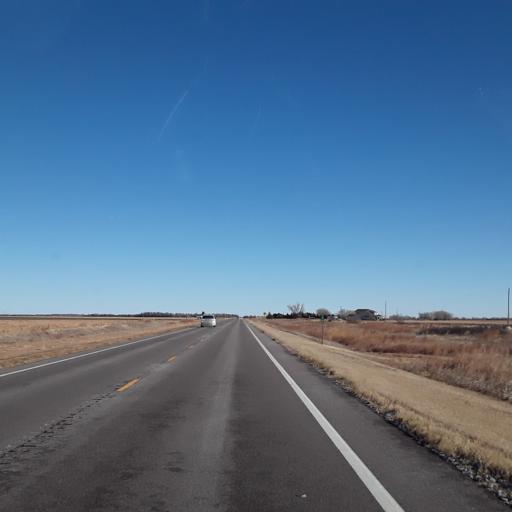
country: US
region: Kansas
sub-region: Pawnee County
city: Larned
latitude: 38.0994
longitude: -99.2089
